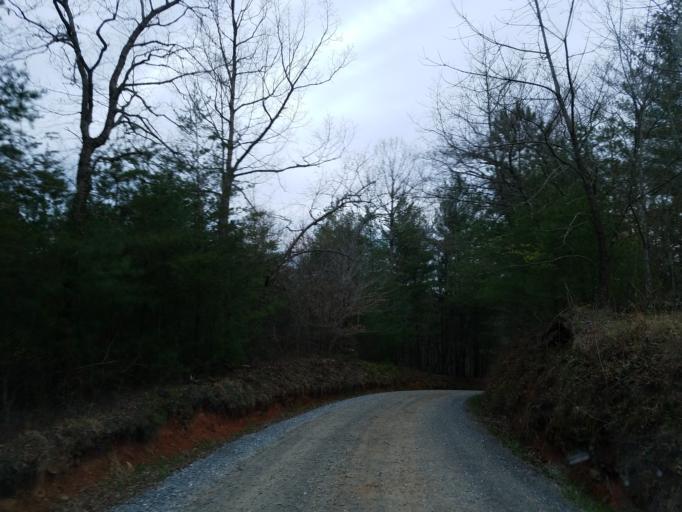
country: US
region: Georgia
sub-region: Gilmer County
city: Ellijay
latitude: 34.6528
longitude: -84.3066
